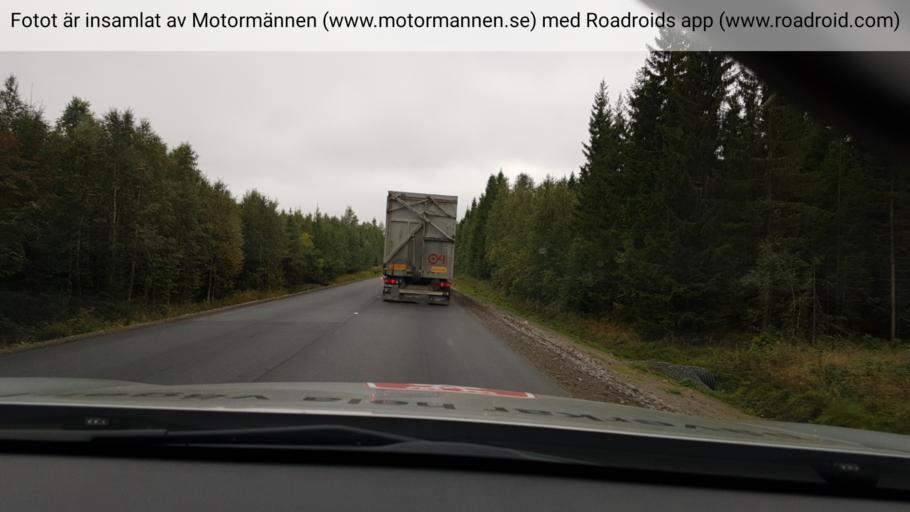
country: SE
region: Vaesterbotten
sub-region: Skelleftea Kommun
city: Burtraesk
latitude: 64.3797
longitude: 20.5127
